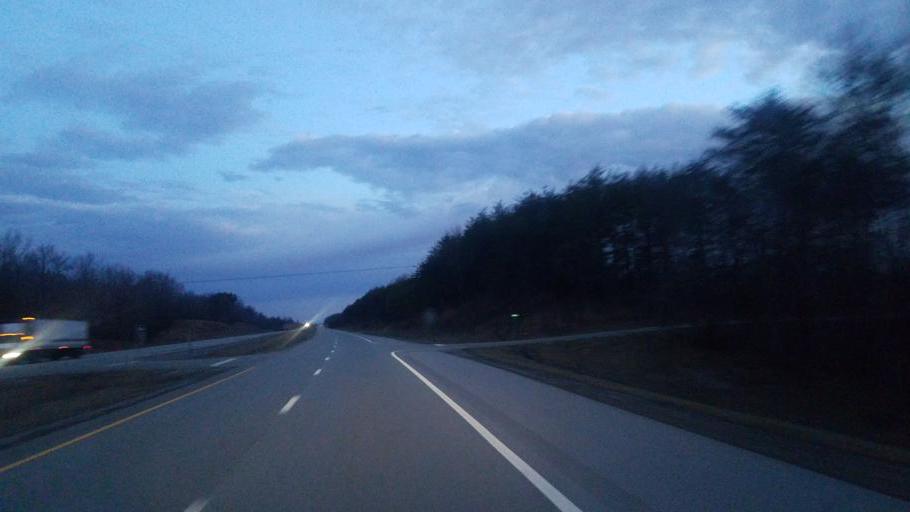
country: US
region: Tennessee
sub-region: Van Buren County
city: Spencer
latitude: 35.6415
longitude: -85.4743
